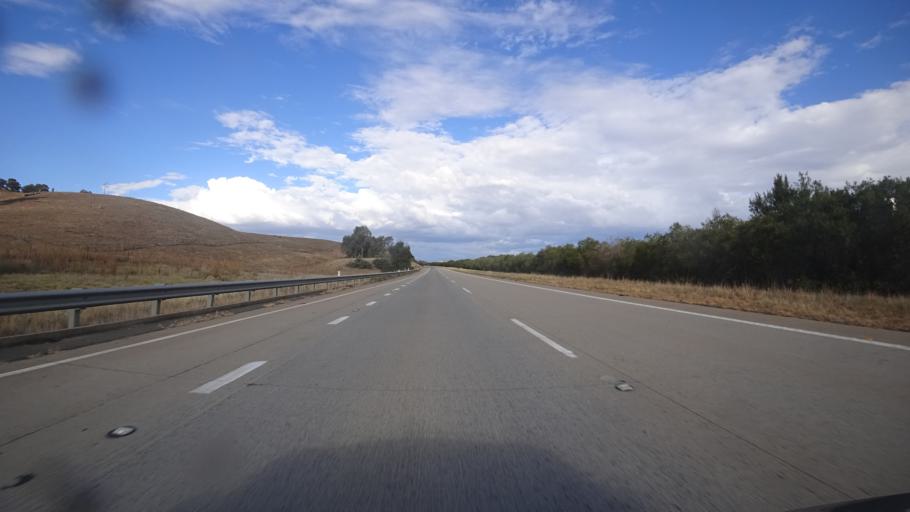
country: AU
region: New South Wales
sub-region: Gundagai
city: Gundagai
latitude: -34.8177
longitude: 148.3584
